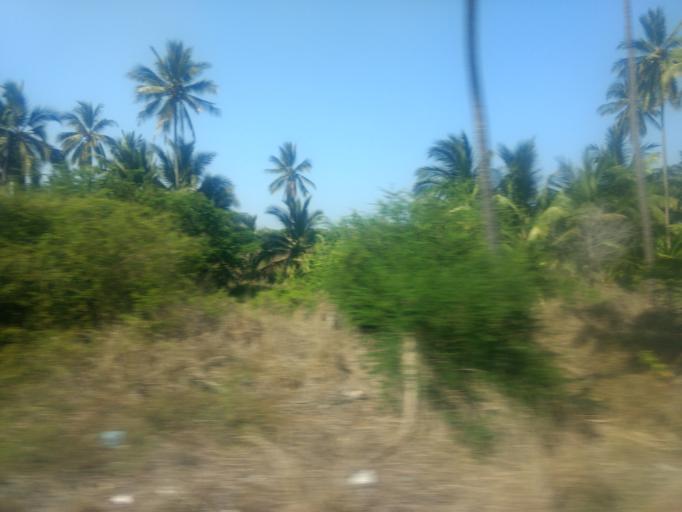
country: MX
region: Colima
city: El Colomo
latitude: 18.9889
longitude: -104.2195
